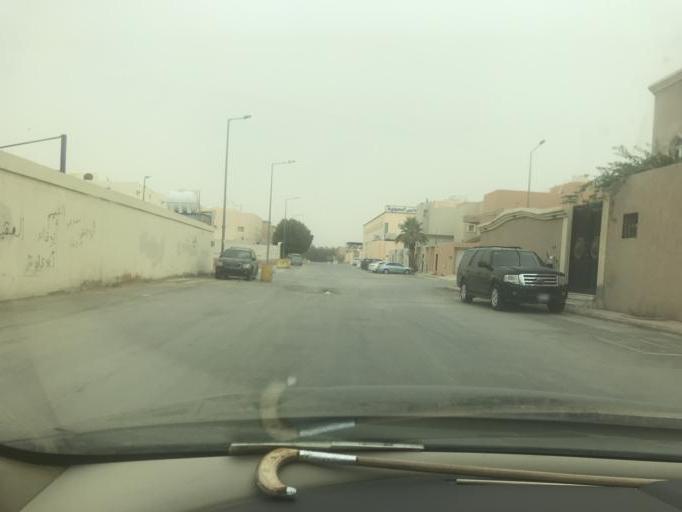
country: SA
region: Ar Riyad
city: Riyadh
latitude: 24.7302
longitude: 46.7891
